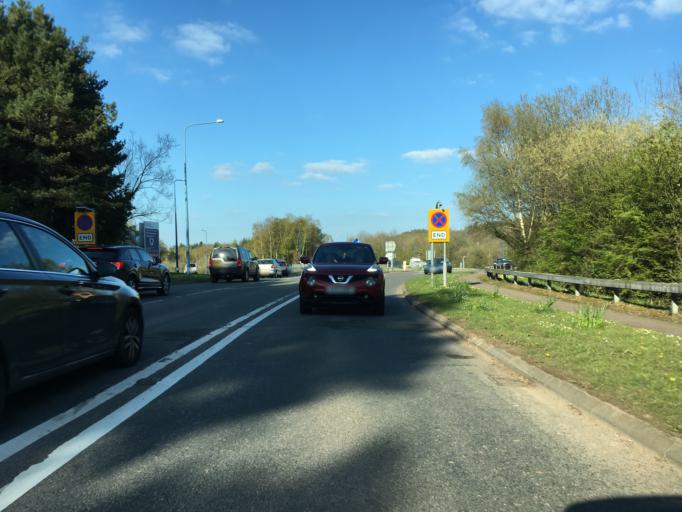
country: GB
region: Wales
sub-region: Torfaen County Borough
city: Cwmbran
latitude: 51.6721
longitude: -3.0203
